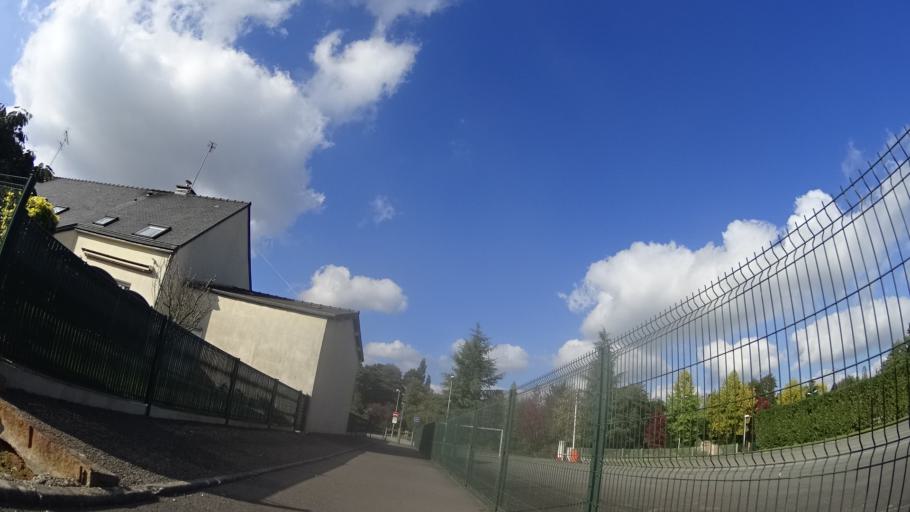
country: FR
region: Brittany
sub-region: Departement d'Ille-et-Vilaine
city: Geveze
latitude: 48.2214
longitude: -1.7866
